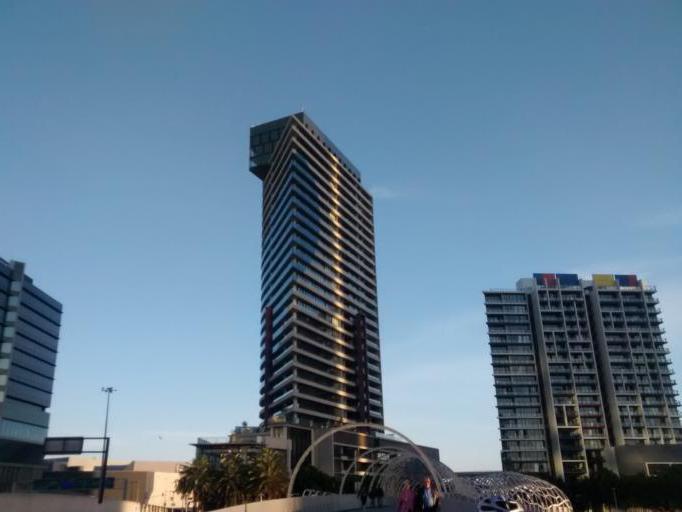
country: AU
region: Victoria
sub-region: Melbourne
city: Docklands
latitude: -37.8231
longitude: 144.9473
